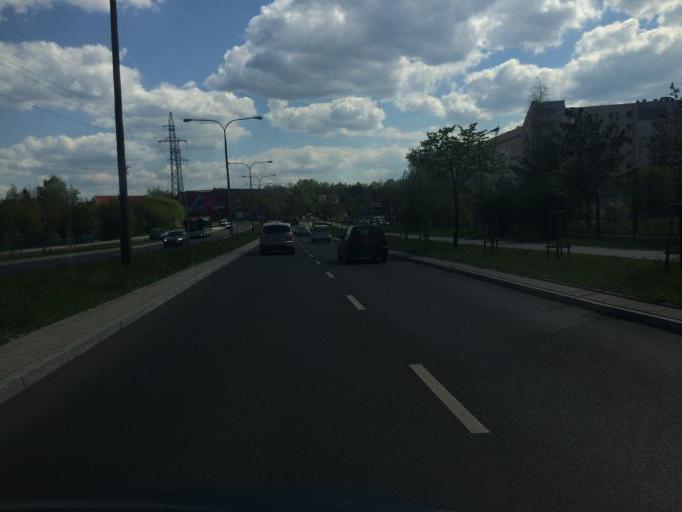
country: PL
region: Warmian-Masurian Voivodeship
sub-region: Olsztyn
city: Kortowo
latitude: 53.7706
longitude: 20.4576
